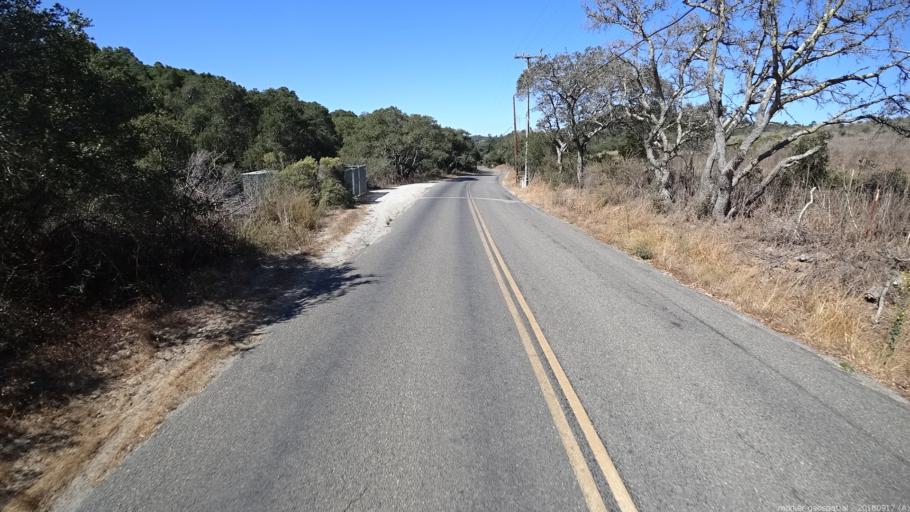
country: US
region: California
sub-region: Monterey County
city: Elkhorn
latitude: 36.8324
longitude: -121.6920
